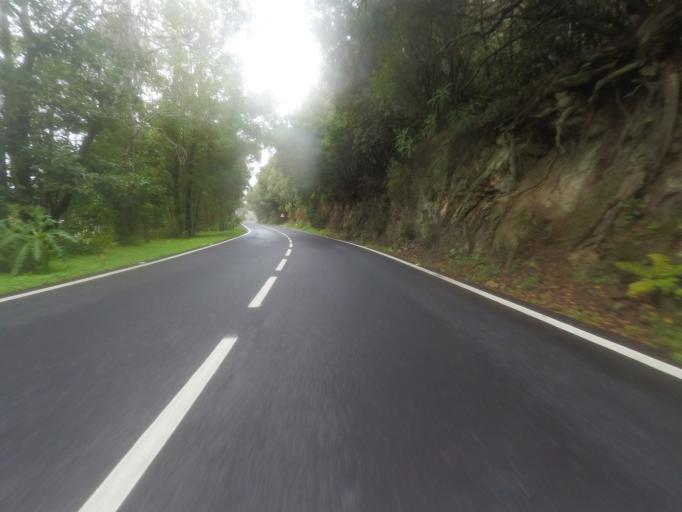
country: ES
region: Canary Islands
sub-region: Provincia de Santa Cruz de Tenerife
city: Alajero
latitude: 28.1182
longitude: -17.2469
